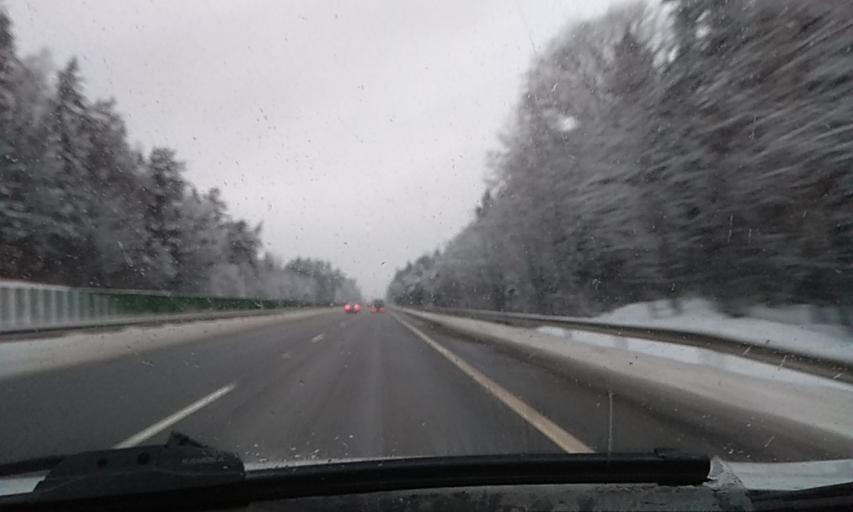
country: LT
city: Trakai
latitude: 54.7236
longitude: 24.9662
